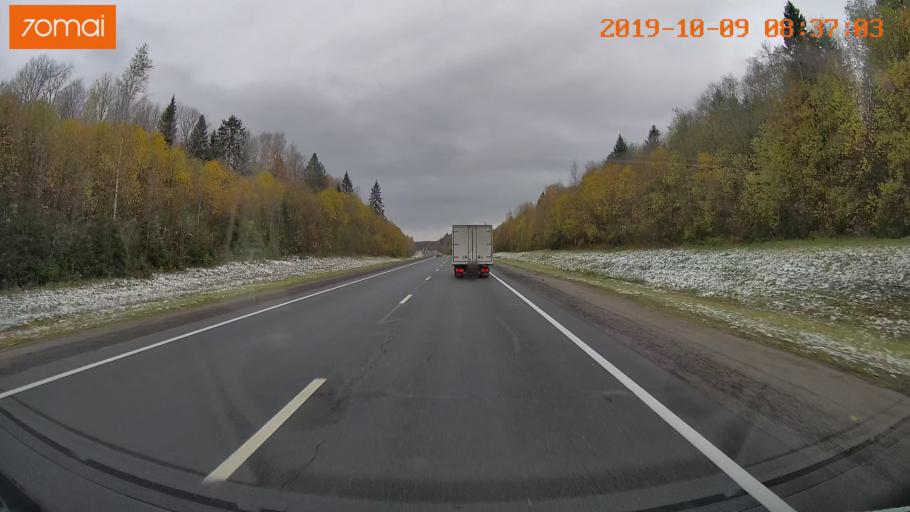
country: RU
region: Vologda
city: Gryazovets
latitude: 58.9354
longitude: 40.1756
